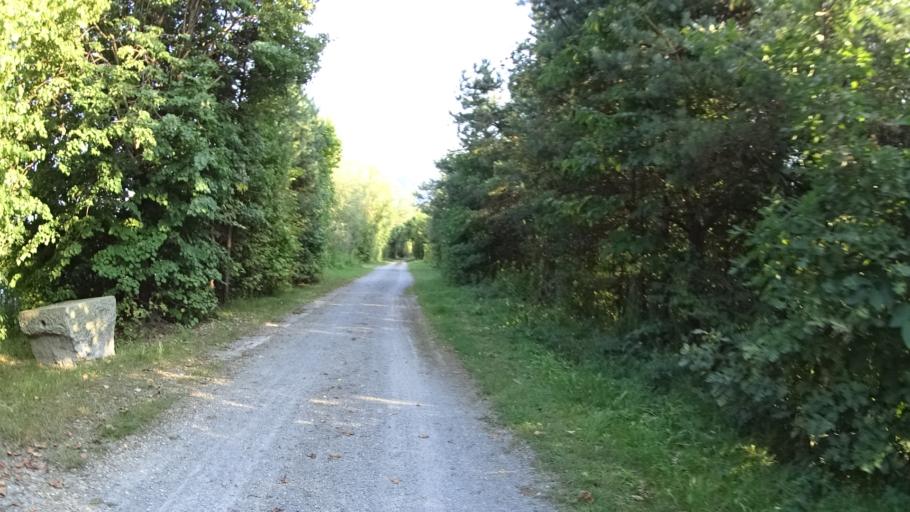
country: AT
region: Carinthia
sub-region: Politischer Bezirk Villach Land
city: Sankt Jakob
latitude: 46.5426
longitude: 14.0891
